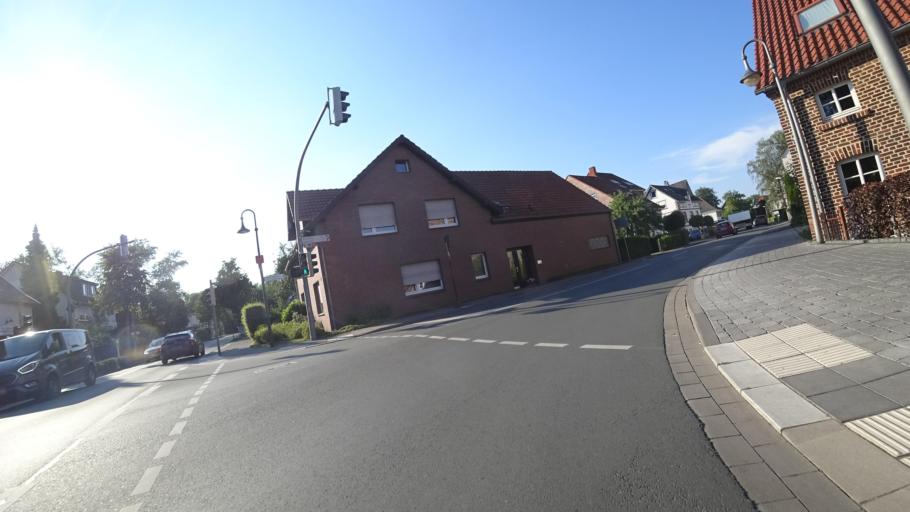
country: DE
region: North Rhine-Westphalia
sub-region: Regierungsbezirk Detmold
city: Guetersloh
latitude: 51.9469
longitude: 8.4083
